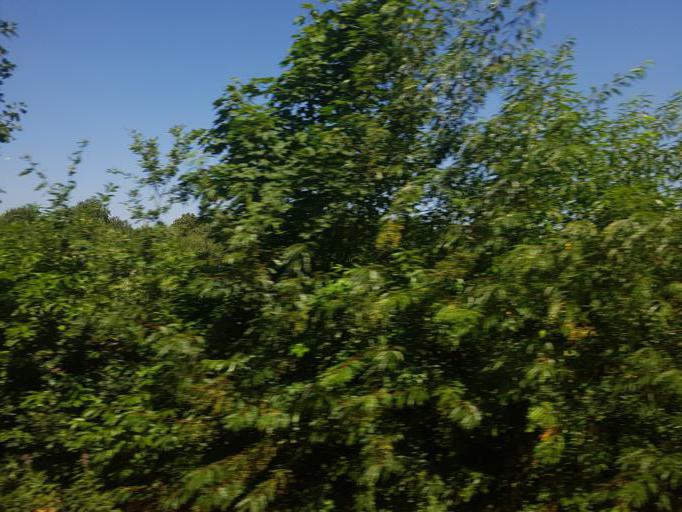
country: NL
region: Utrecht
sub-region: Gemeente De Bilt
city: De Bilt
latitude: 52.1227
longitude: 5.1766
